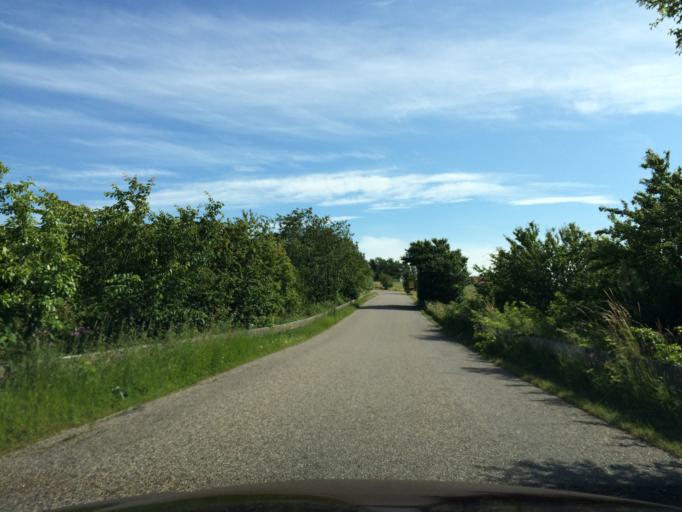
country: DK
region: Central Jutland
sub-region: Silkeborg Kommune
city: Silkeborg
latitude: 56.2117
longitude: 9.5622
